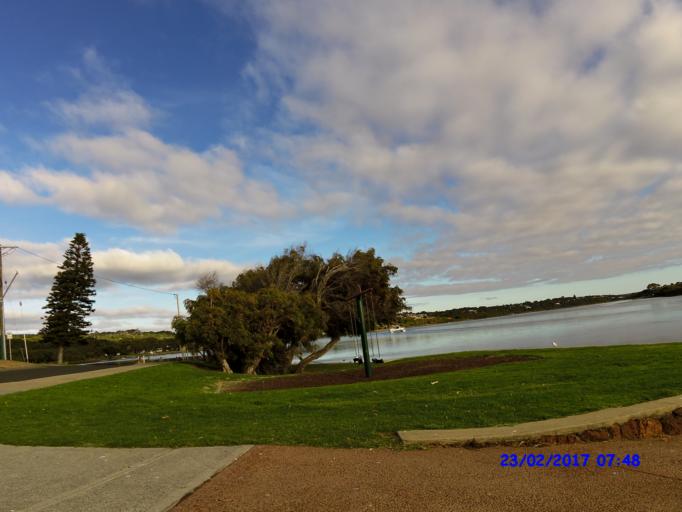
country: AU
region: Western Australia
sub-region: Augusta-Margaret River Shire
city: Augusta
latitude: -34.3244
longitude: 115.1693
